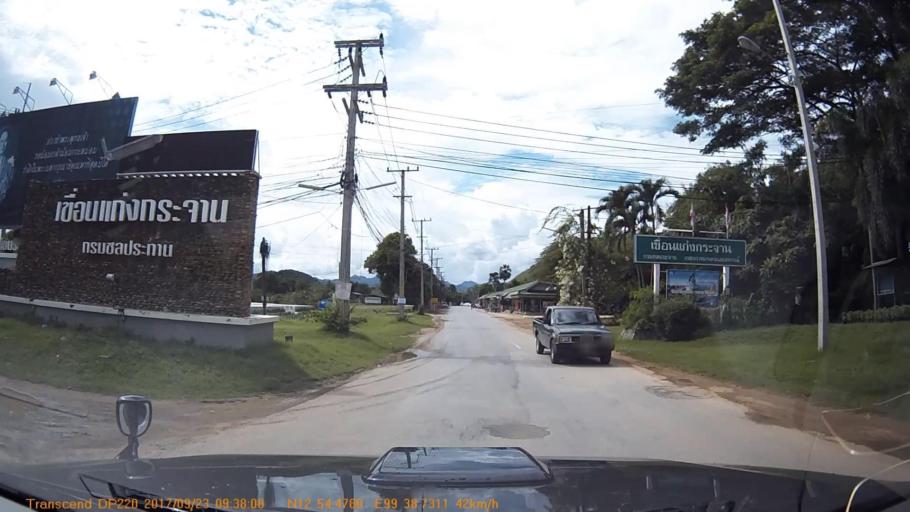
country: TH
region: Phetchaburi
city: Kaeng Krachan
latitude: 12.9081
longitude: 99.6453
